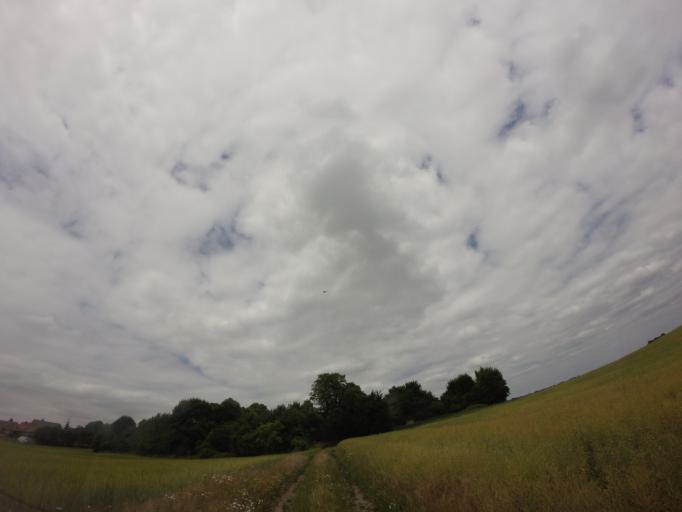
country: PL
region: West Pomeranian Voivodeship
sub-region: Powiat choszczenski
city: Krzecin
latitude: 53.0732
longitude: 15.5269
